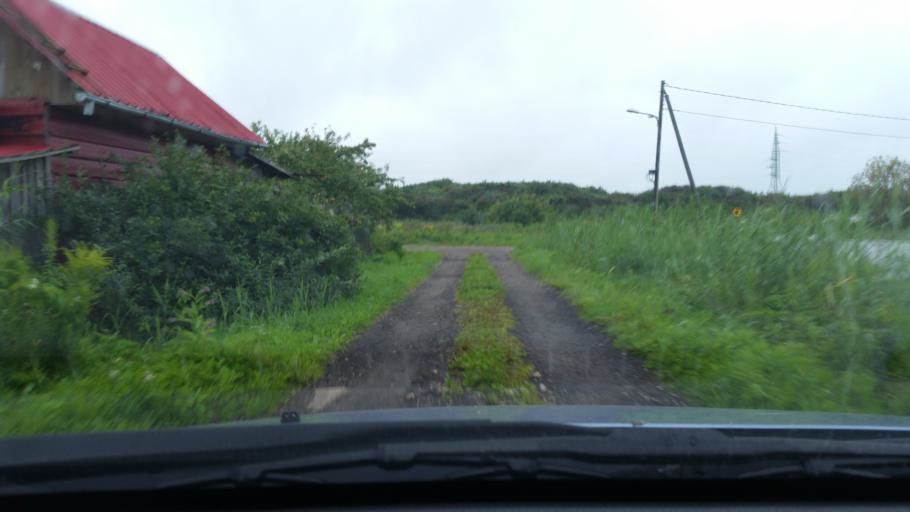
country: LV
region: Riga
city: Bolderaja
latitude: 57.0003
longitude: 24.0350
